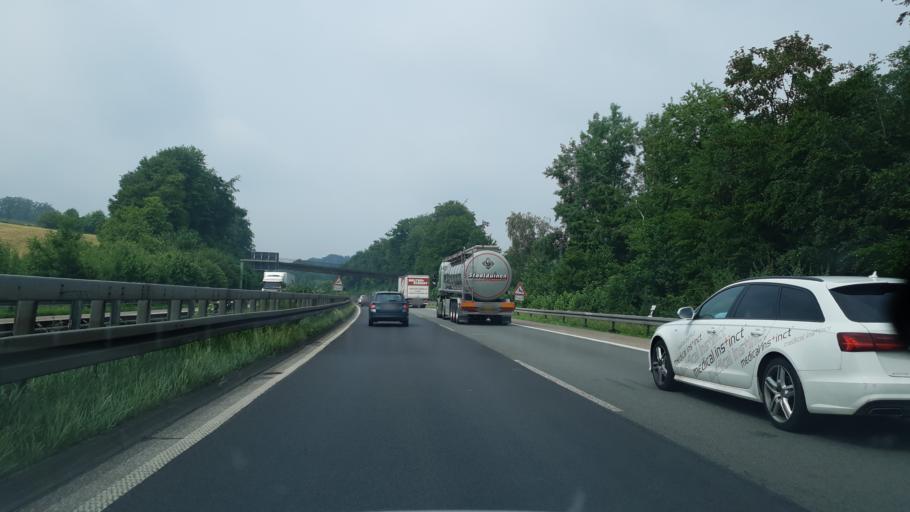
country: DE
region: North Rhine-Westphalia
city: Sprockhovel
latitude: 51.3667
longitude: 7.2752
